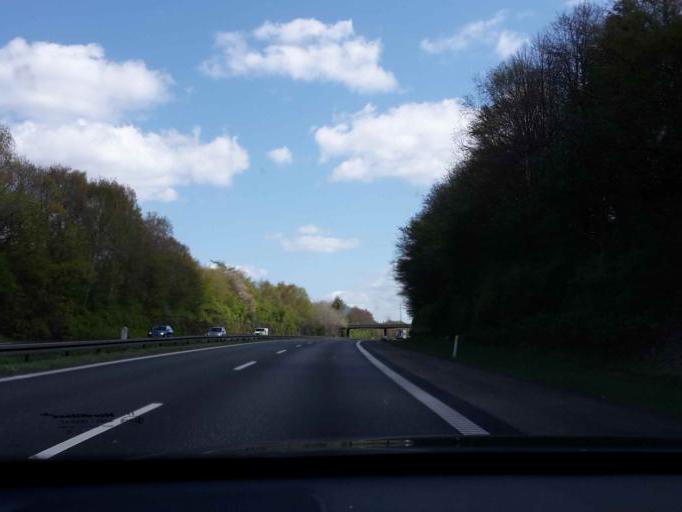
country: DK
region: South Denmark
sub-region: Fredericia Kommune
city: Taulov
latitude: 55.5424
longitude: 9.6072
